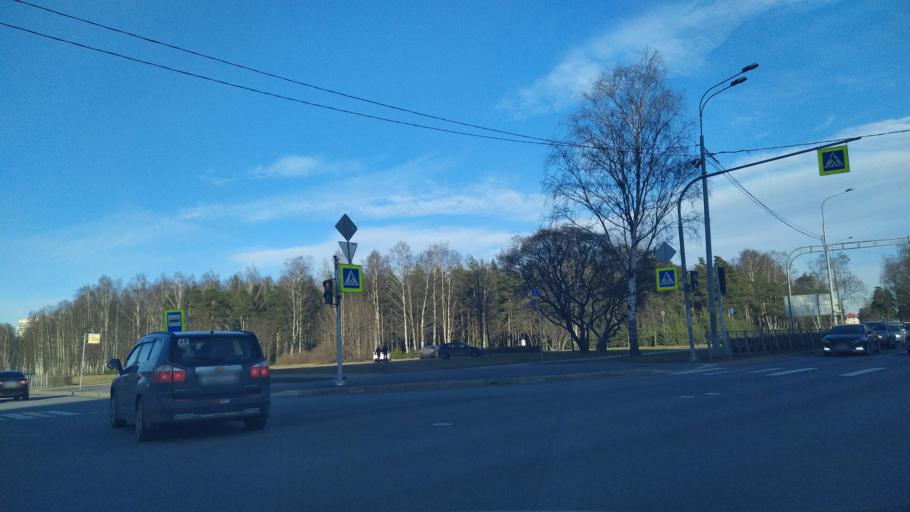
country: RU
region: Leningrad
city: Kalininskiy
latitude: 59.9947
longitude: 30.3913
